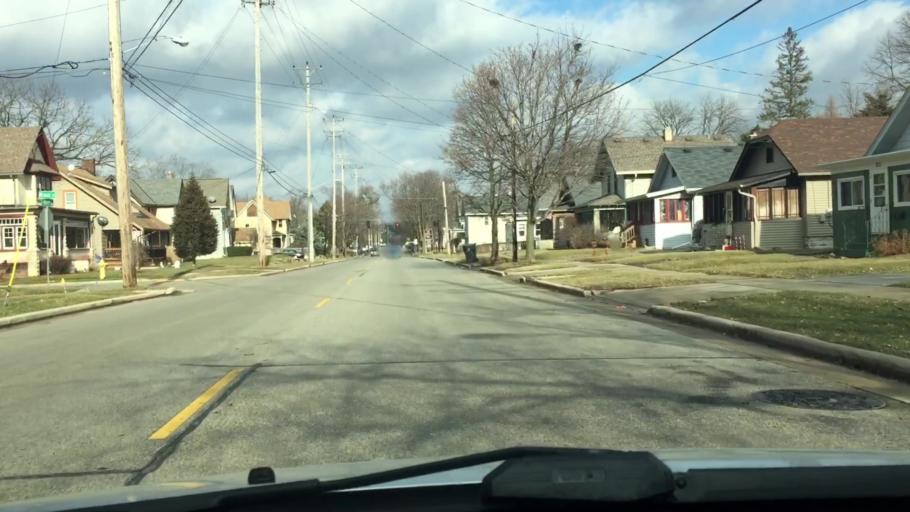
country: US
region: Wisconsin
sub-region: Waukesha County
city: Waukesha
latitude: 43.0013
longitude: -88.2368
